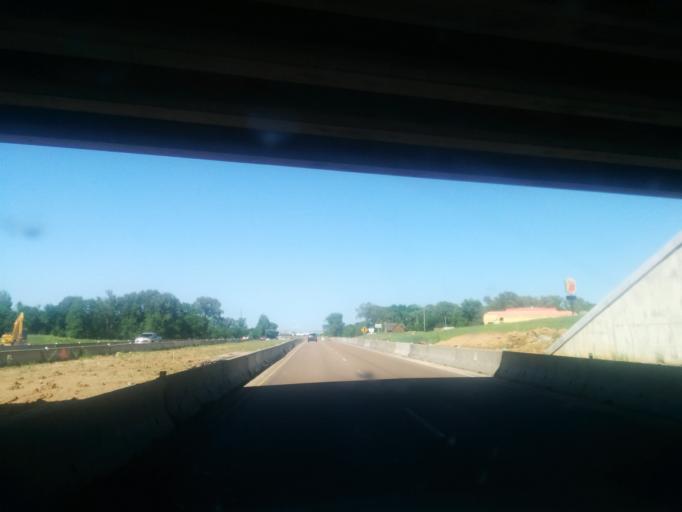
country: US
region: Mississippi
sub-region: Madison County
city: Madison
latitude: 32.5172
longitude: -90.1014
